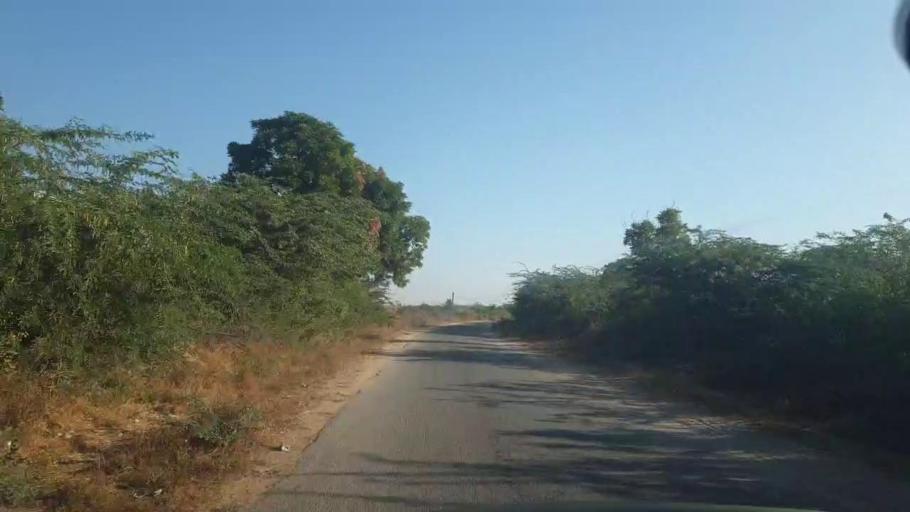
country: PK
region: Sindh
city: Malir Cantonment
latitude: 25.1055
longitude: 67.2598
